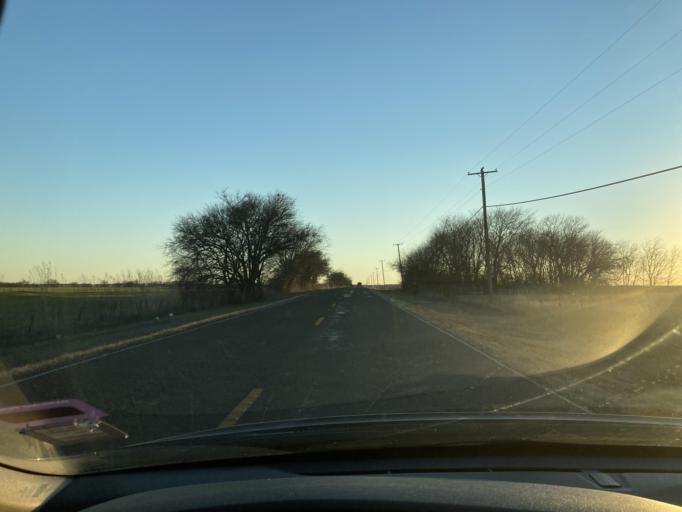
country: US
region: Texas
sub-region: Ellis County
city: Waxahachie
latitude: 32.3677
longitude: -96.8627
